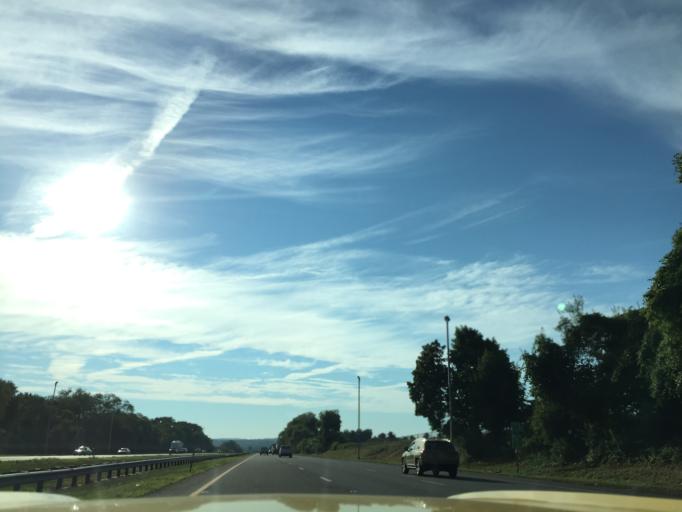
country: US
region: New Jersey
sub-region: Hunterdon County
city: Clinton
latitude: 40.6330
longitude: -74.9366
